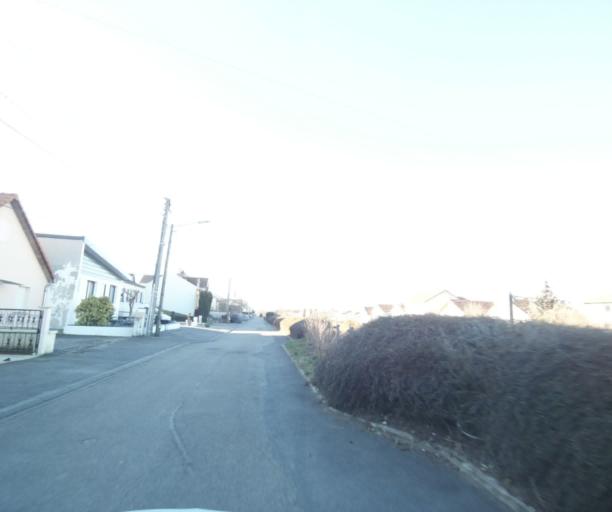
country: FR
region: Lorraine
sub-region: Departement de Meurthe-et-Moselle
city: Laneuveville-devant-Nancy
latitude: 48.6494
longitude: 6.2377
